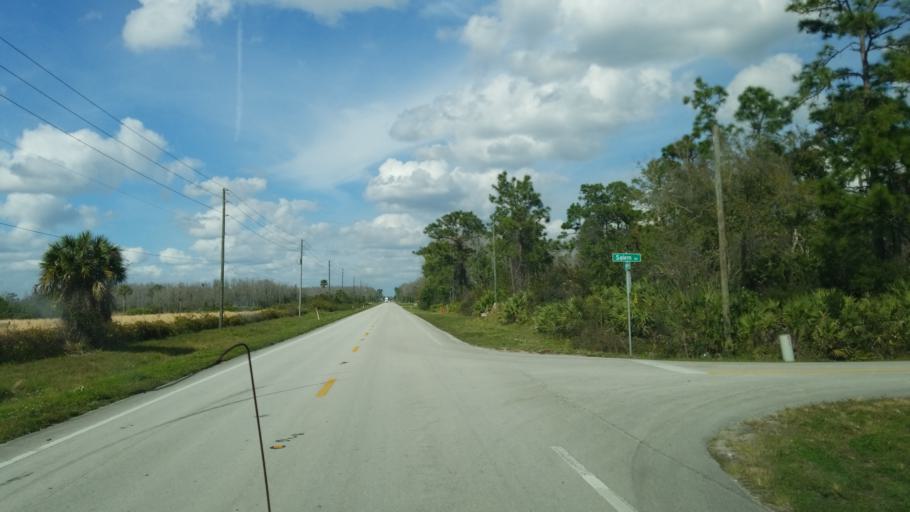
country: US
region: Florida
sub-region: Osceola County
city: Saint Cloud
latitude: 28.1237
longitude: -81.0763
